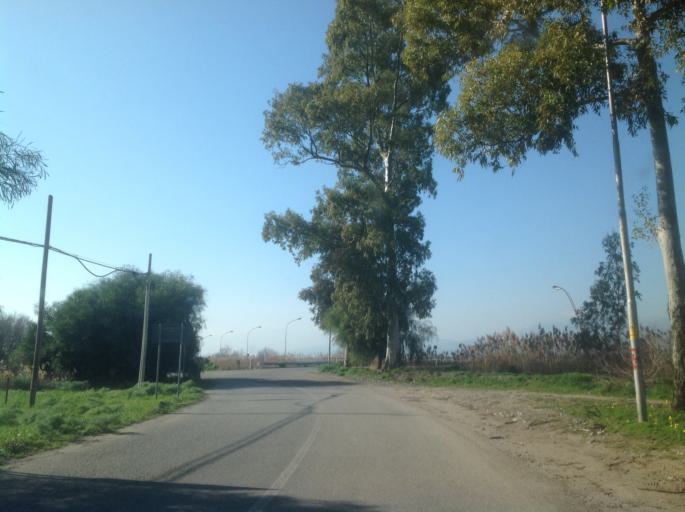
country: IT
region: Calabria
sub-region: Provincia di Cosenza
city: Sibari
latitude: 39.7270
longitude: 16.4970
